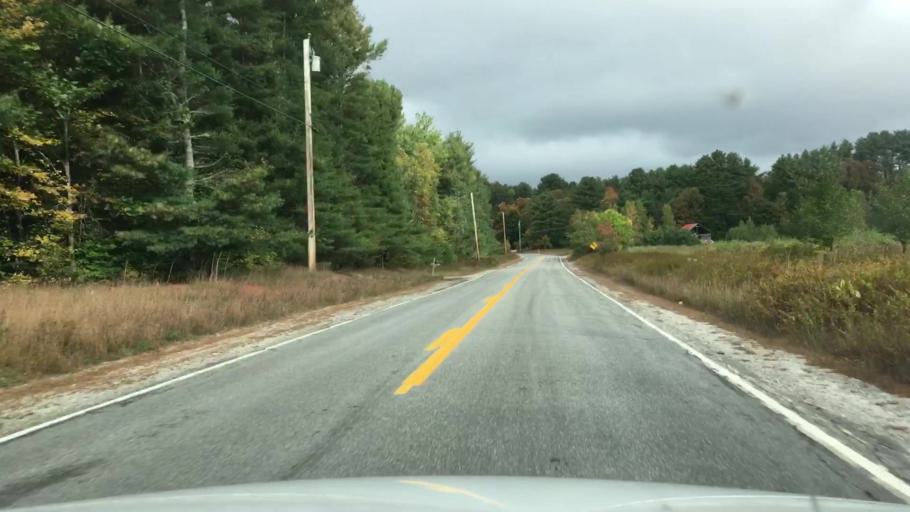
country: US
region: Maine
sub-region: Oxford County
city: Bethel
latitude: 44.3370
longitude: -70.7797
